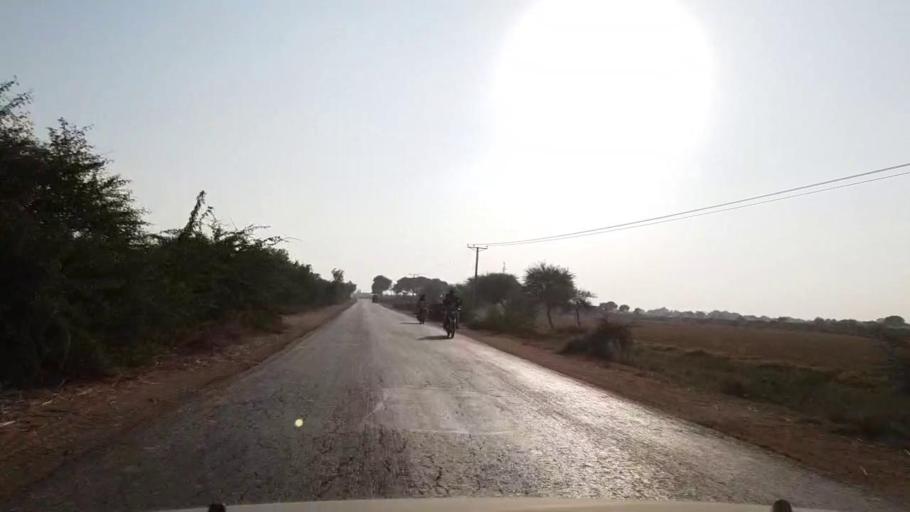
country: PK
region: Sindh
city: Mirpur Batoro
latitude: 24.7437
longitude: 68.2614
